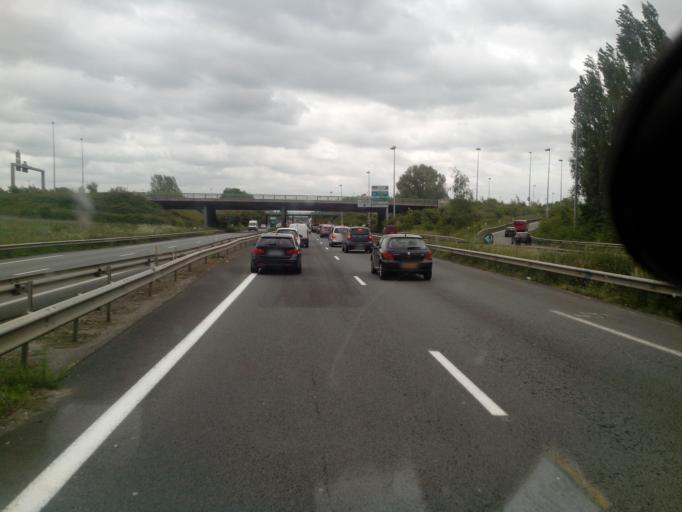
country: FR
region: Nord-Pas-de-Calais
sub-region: Departement du Nord
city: Hallennes-lez-Haubourdin
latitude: 50.6294
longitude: 2.9576
